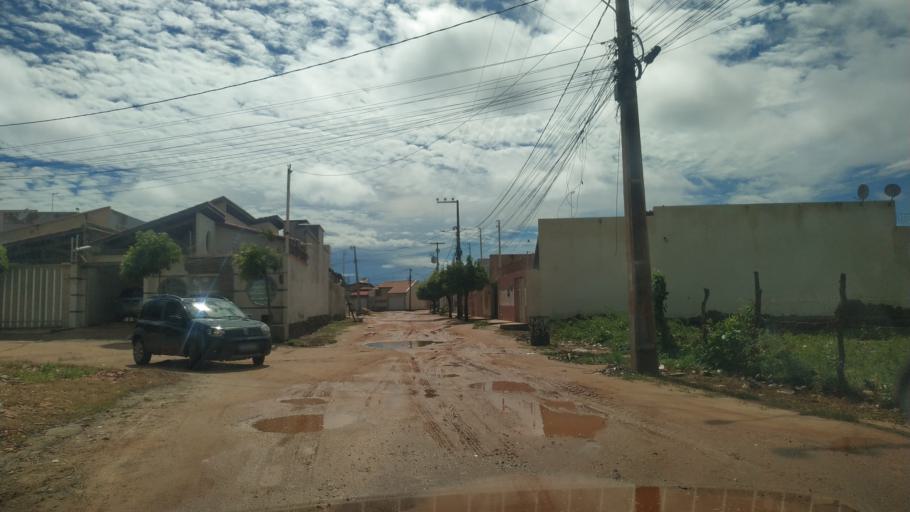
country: BR
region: Rio Grande do Norte
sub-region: Areia Branca
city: Areia Branca
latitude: -4.9541
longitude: -37.1233
